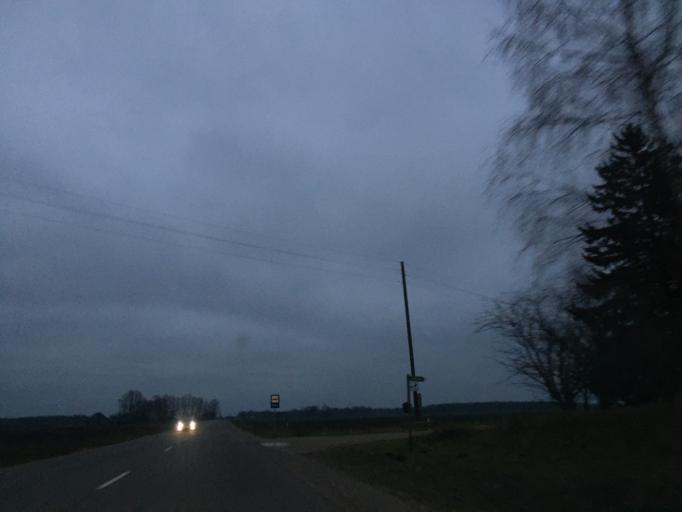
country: LV
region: Koceni
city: Koceni
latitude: 57.5479
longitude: 25.2785
